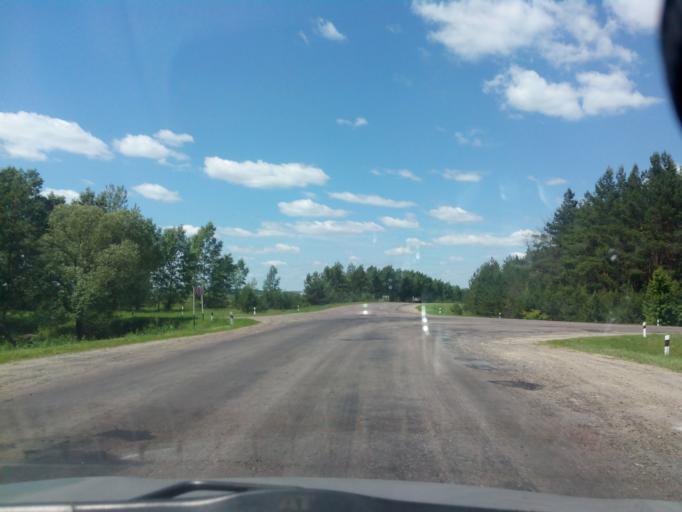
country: RU
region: Voronezj
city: Ternovka
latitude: 51.7169
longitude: 41.5187
